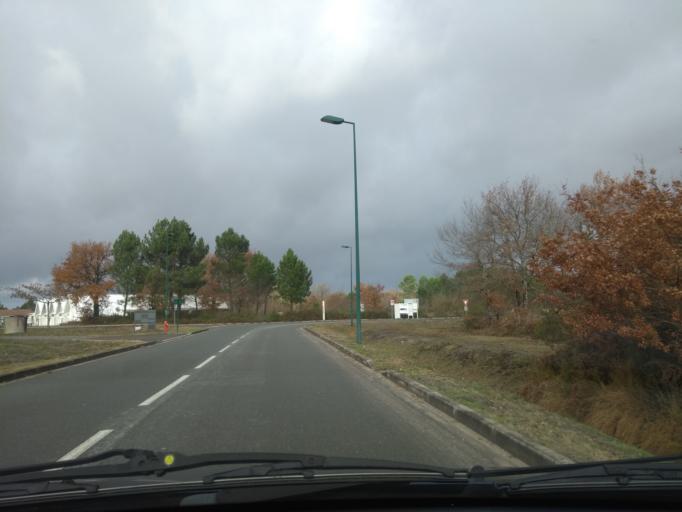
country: FR
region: Aquitaine
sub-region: Departement de la Gironde
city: Belin-Beliet
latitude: 44.5275
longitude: -0.8172
